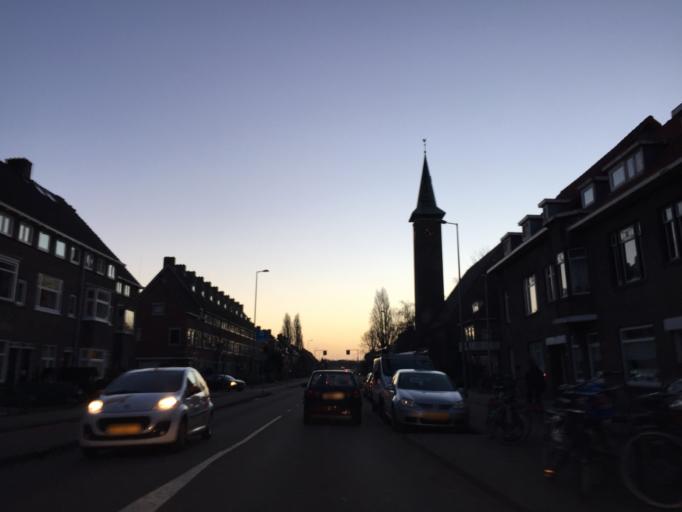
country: NL
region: South Holland
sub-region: Gemeente Rotterdam
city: Rotterdam
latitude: 51.9449
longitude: 4.4738
